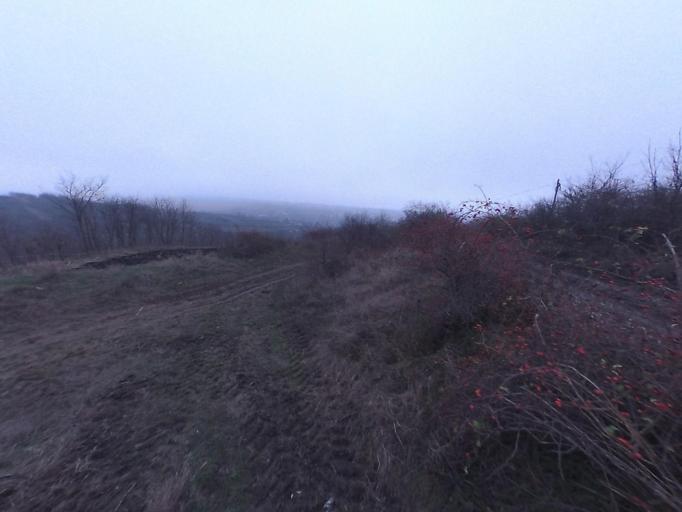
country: RO
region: Galati
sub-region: Comuna Balabanesti
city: Balabanesti
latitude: 46.1454
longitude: 27.7402
